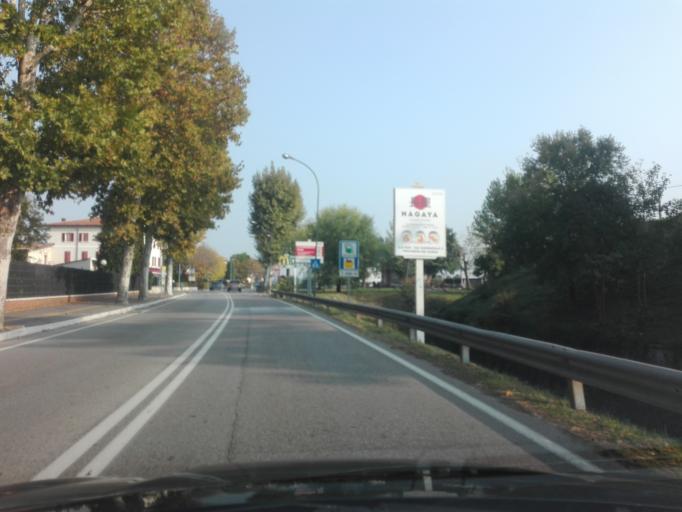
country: IT
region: Veneto
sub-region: Provincia di Verona
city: Peschiera del Garda
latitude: 45.4411
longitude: 10.6800
